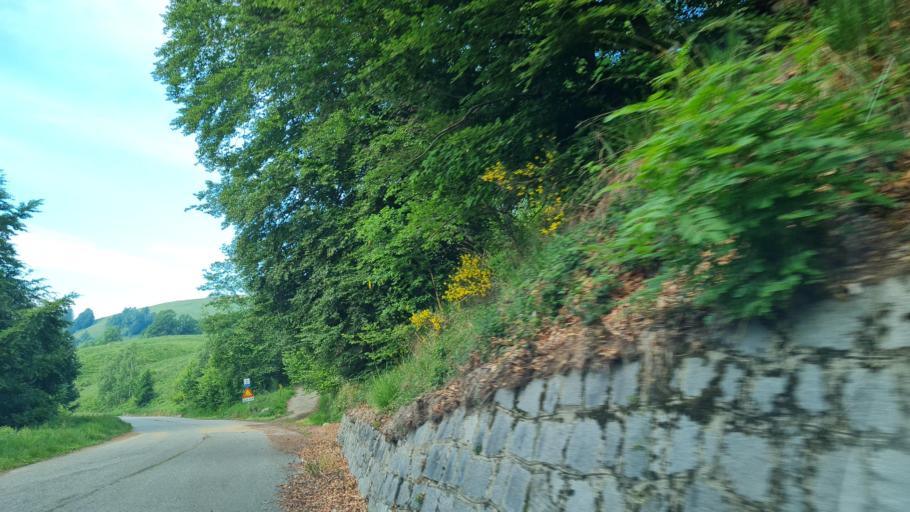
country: IT
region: Piedmont
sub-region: Provincia di Biella
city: Sordevolo
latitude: 45.6139
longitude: 7.9822
